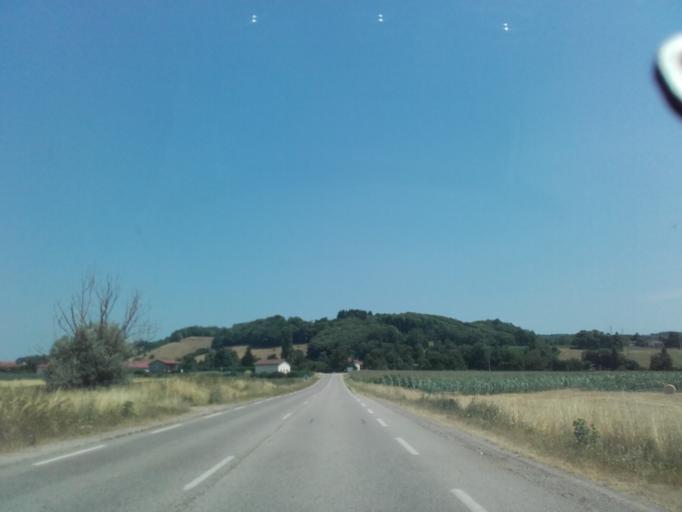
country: FR
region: Rhone-Alpes
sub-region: Departement de l'Isere
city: Champier
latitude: 45.4412
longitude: 5.2899
